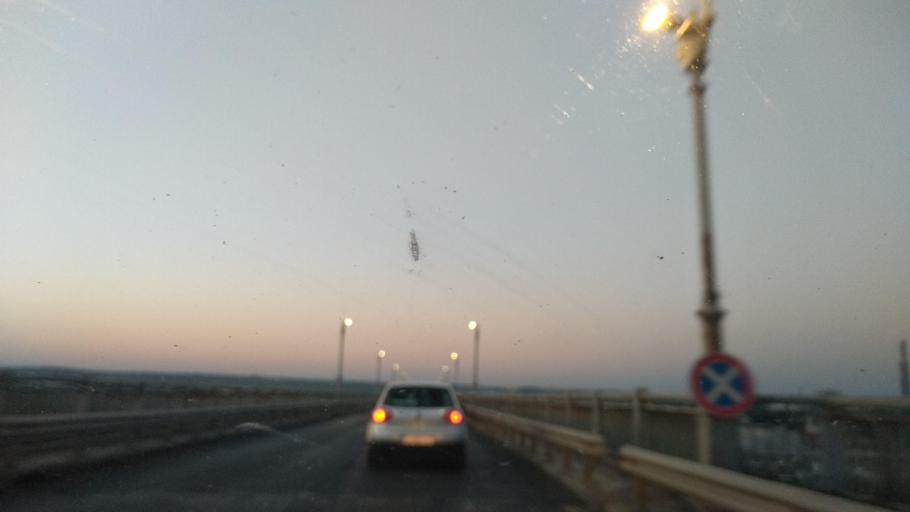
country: RO
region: Giurgiu
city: Giurgiu
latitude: 43.8857
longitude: 26.0090
